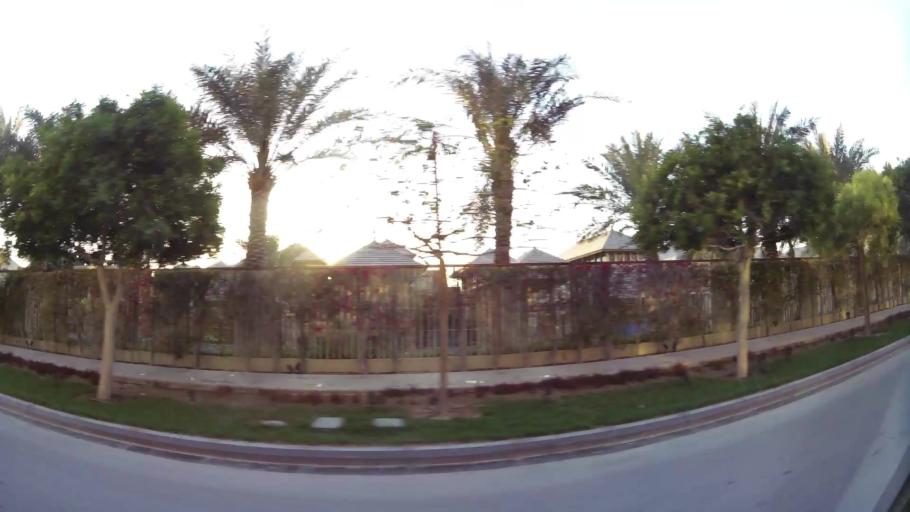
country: BH
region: Manama
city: Jidd Hafs
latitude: 26.2424
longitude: 50.5673
